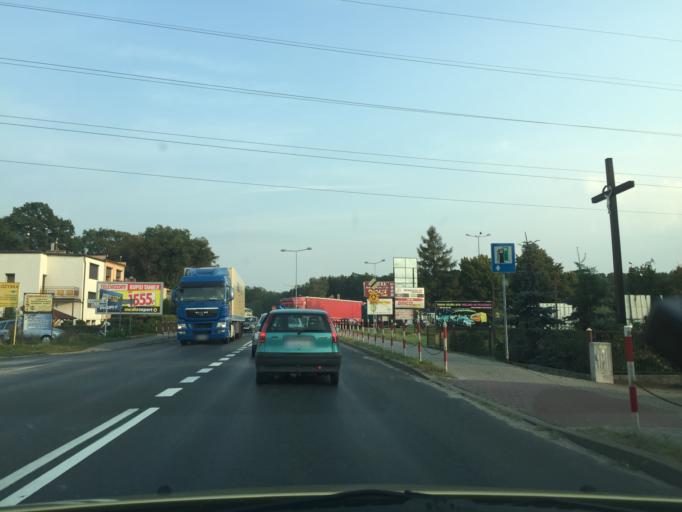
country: PL
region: Greater Poland Voivodeship
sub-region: Powiat jarocinski
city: Jarocin
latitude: 51.9571
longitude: 17.5179
